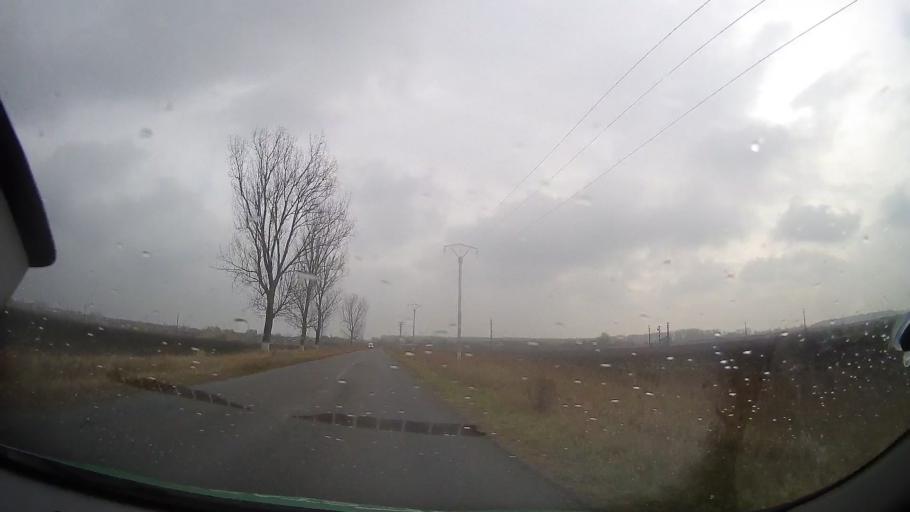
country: RO
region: Prahova
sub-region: Comuna Draganesti
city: Draganesti
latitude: 44.8318
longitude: 26.2742
